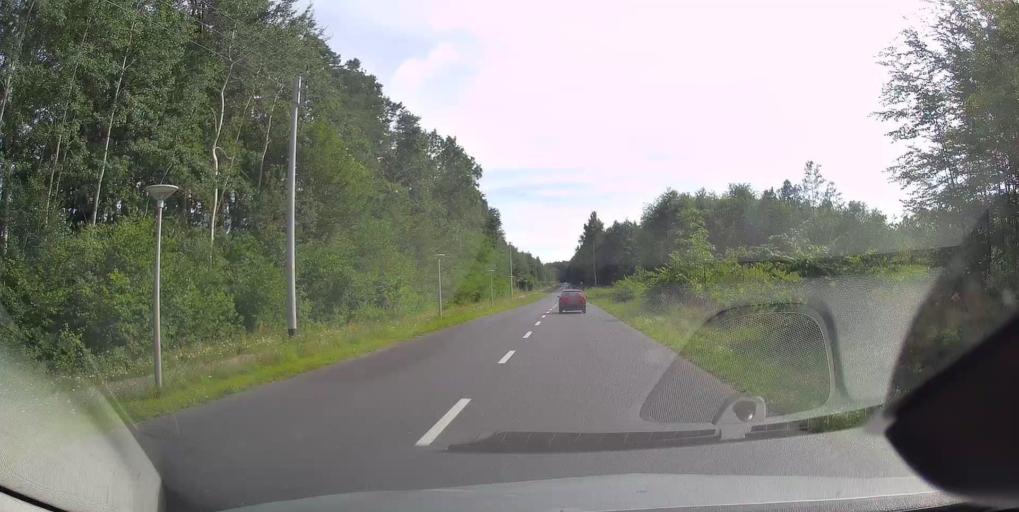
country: PL
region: Lodz Voivodeship
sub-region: Powiat tomaszowski
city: Tomaszow Mazowiecki
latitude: 51.5092
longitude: 19.9985
